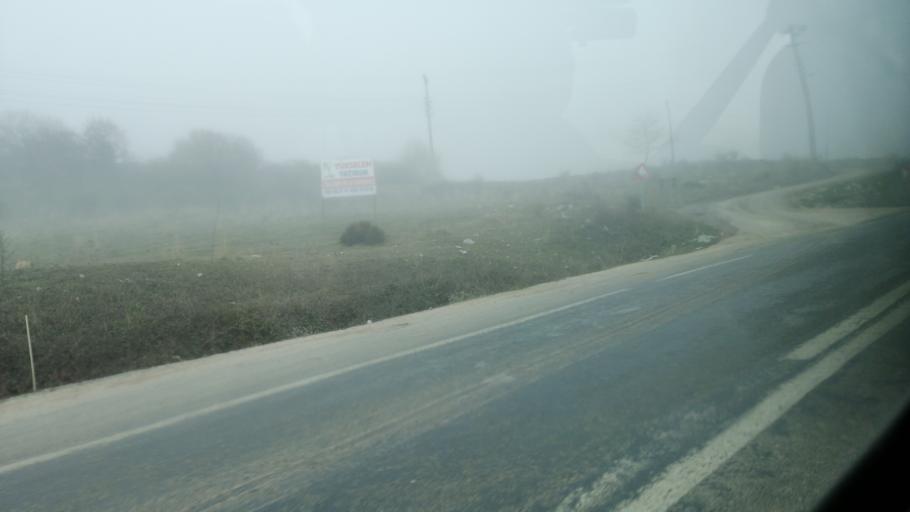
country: TR
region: Yalova
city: Kadikoy
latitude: 40.6504
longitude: 29.2017
